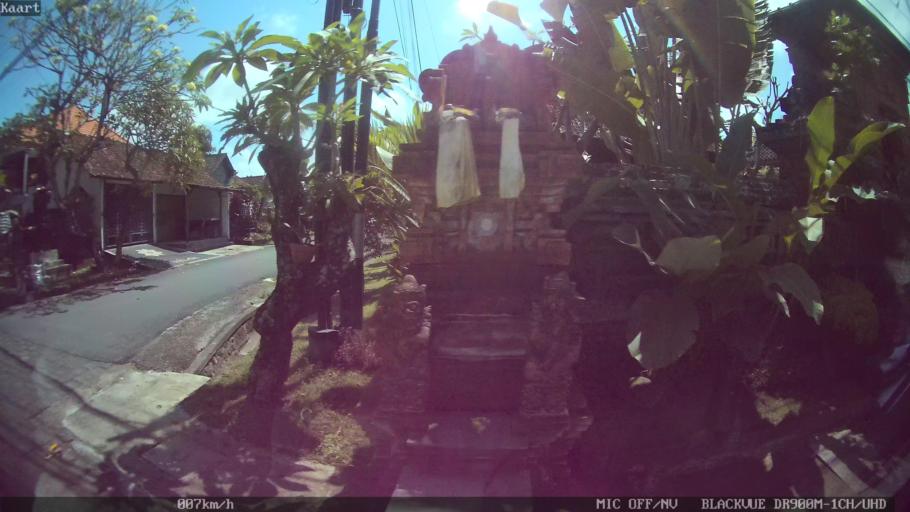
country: ID
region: Bali
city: Banjar Paangkelod
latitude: -8.6120
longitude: 115.2549
